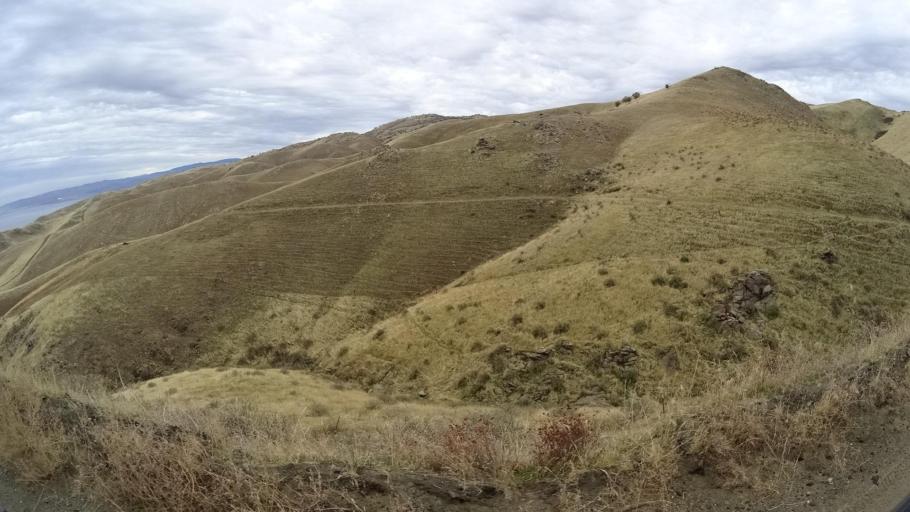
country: US
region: California
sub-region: Kern County
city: Arvin
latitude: 35.1335
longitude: -118.7705
